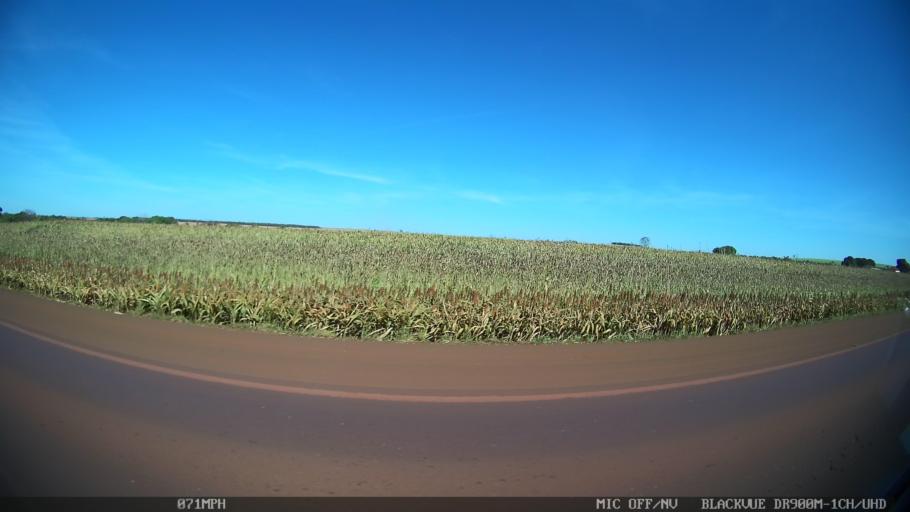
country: BR
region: Sao Paulo
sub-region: Ipua
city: Ipua
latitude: -20.4921
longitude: -47.9918
